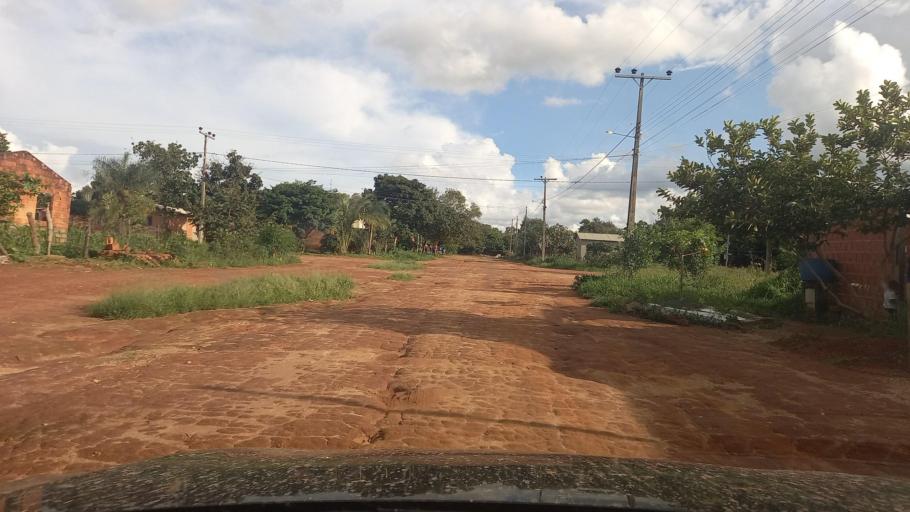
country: BR
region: Goias
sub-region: Cavalcante
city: Cavalcante
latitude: -13.7980
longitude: -47.4410
